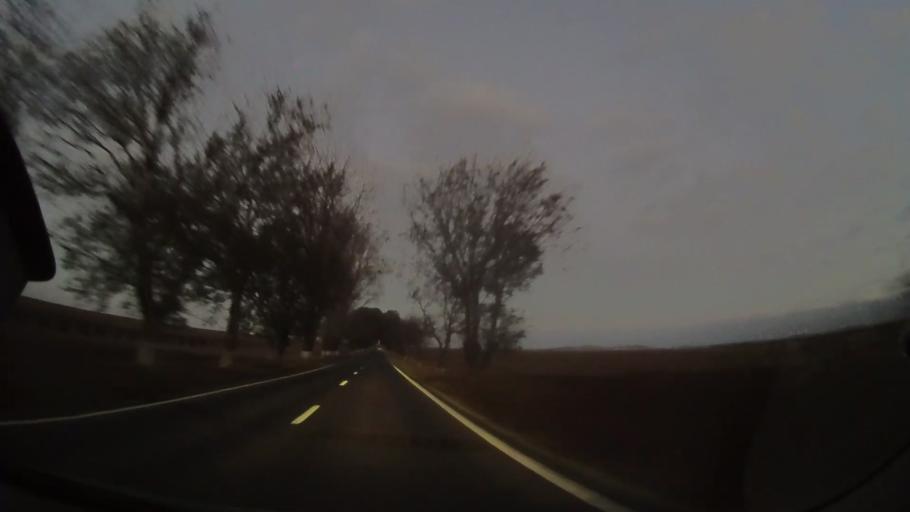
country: RO
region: Tulcea
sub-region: Comuna Frecatei
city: Frecatei
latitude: 45.0809
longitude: 28.6905
